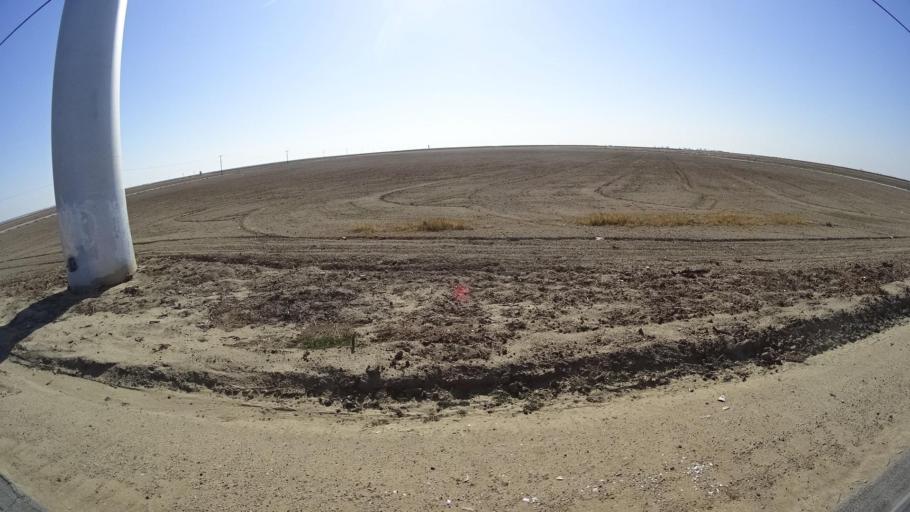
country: US
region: California
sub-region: Kern County
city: McFarland
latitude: 35.7179
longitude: -119.1708
